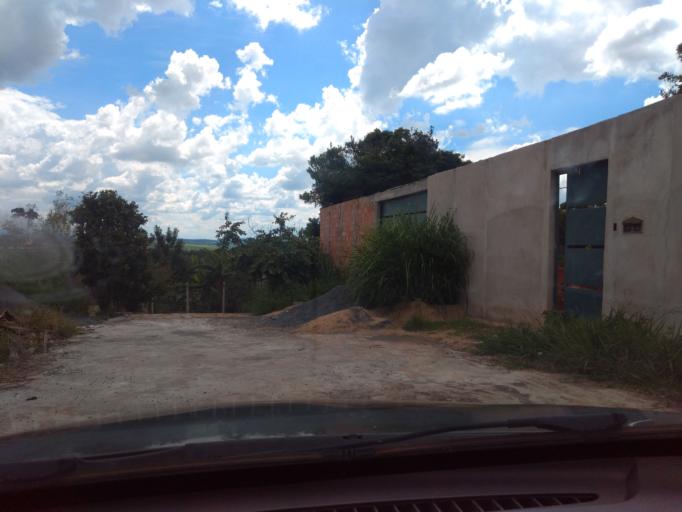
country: BR
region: Minas Gerais
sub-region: Tres Coracoes
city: Tres Coracoes
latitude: -21.6907
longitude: -45.2636
